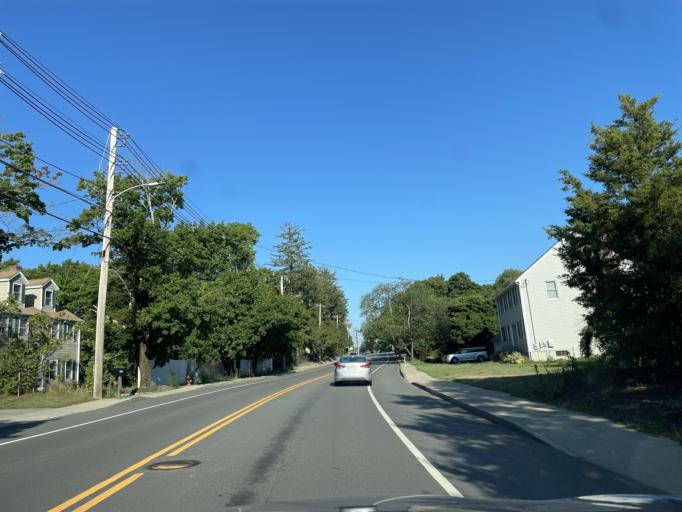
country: US
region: Massachusetts
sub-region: Bristol County
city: Mansfield
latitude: 42.0325
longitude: -71.1925
